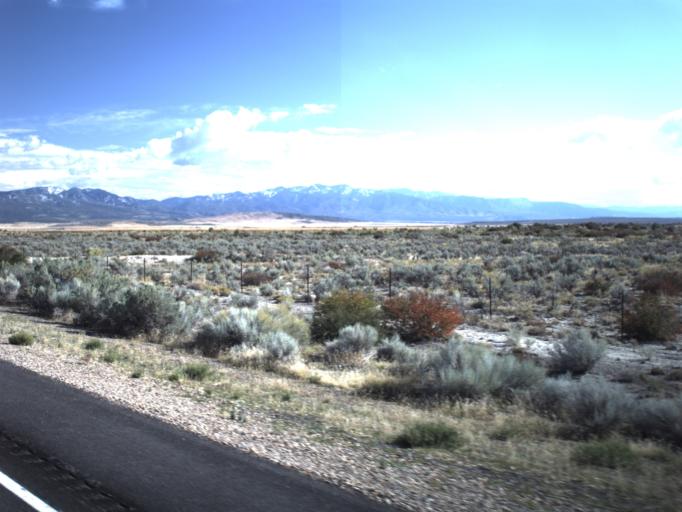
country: US
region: Utah
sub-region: Millard County
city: Fillmore
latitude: 39.1484
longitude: -112.3923
